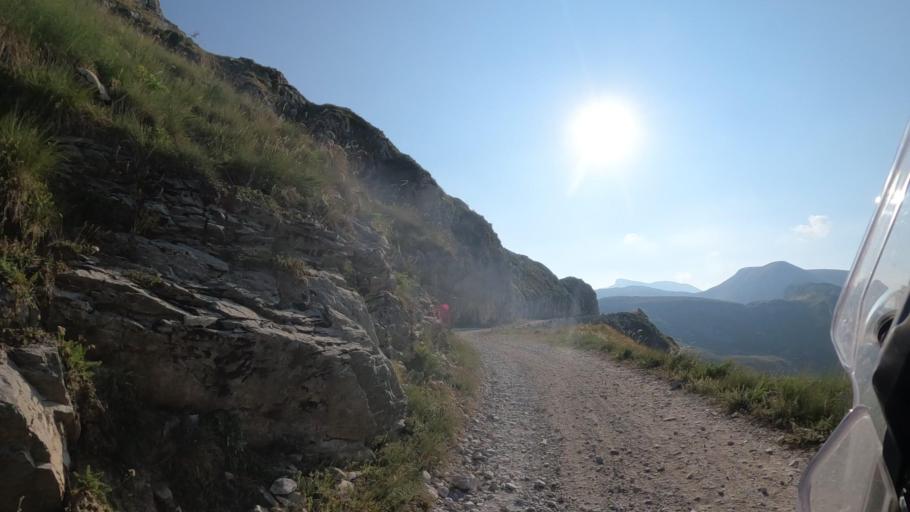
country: IT
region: Piedmont
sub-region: Provincia di Cuneo
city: Limone Piemonte
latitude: 44.1710
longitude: 7.6344
